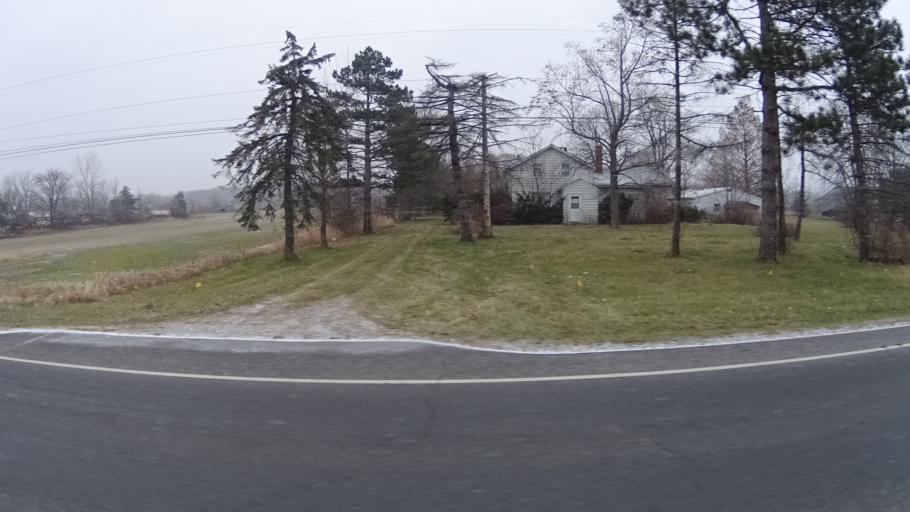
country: US
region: Ohio
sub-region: Lorain County
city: Oberlin
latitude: 41.3131
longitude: -82.2168
